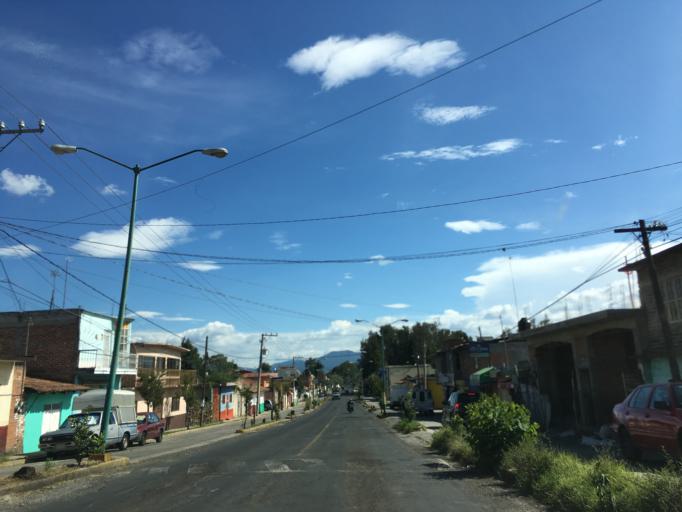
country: MX
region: Michoacan
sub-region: Jimenez
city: Villa Jimenez
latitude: 19.8815
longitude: -101.7735
